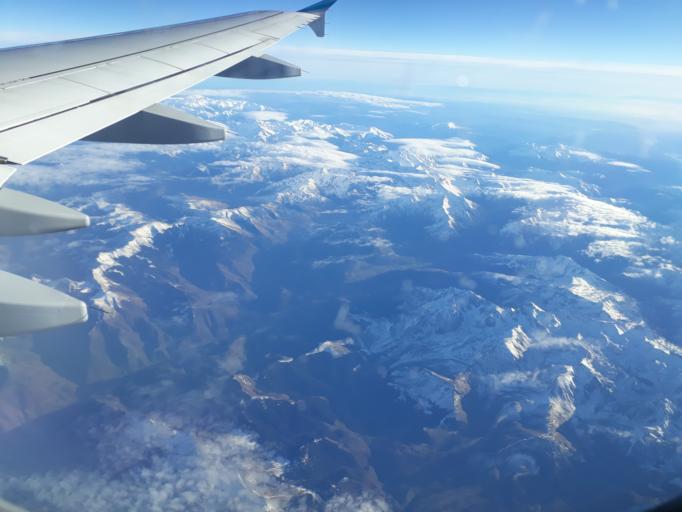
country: FR
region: Midi-Pyrenees
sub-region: Departement des Hautes-Pyrenees
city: Campan
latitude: 43.0430
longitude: 0.2141
